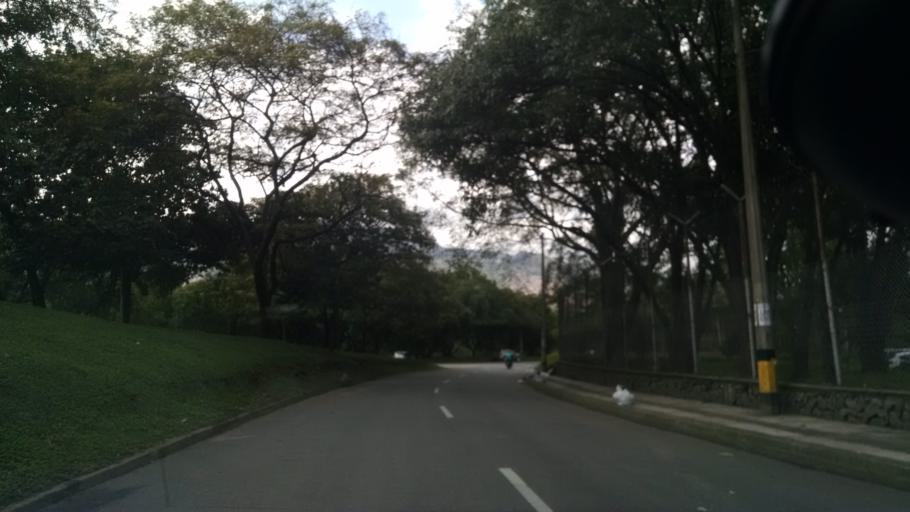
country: CO
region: Antioquia
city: Medellin
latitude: 6.2659
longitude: -75.5709
